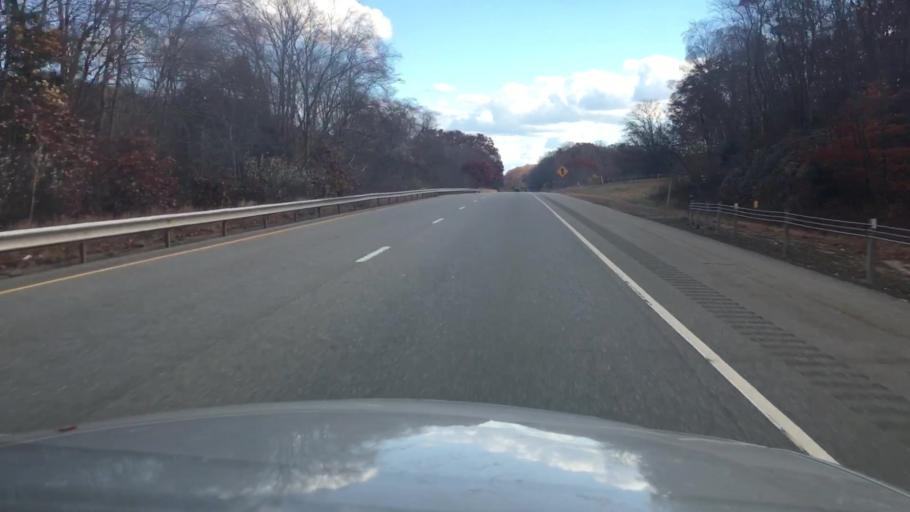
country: US
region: Connecticut
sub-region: Middlesex County
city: Deep River Center
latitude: 41.3622
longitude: -72.4254
